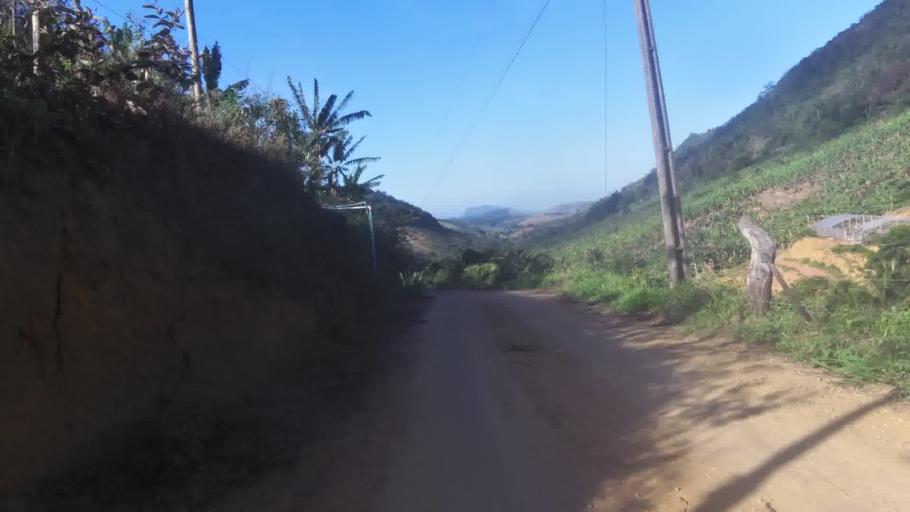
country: BR
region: Espirito Santo
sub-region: Iconha
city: Iconha
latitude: -20.7495
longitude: -40.8006
